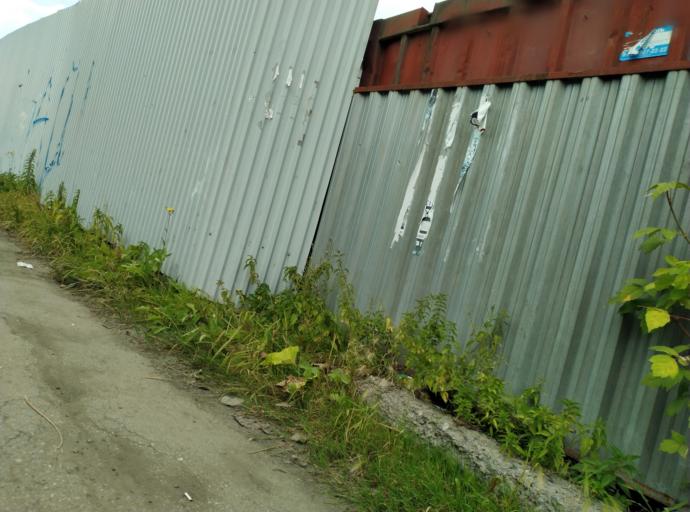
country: RU
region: Tomsk
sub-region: Tomskiy Rayon
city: Tomsk
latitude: 56.5254
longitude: 84.9585
